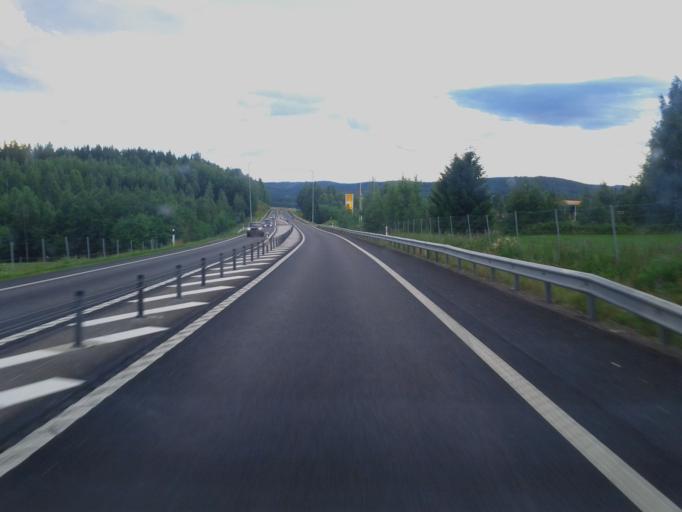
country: SE
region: Dalarna
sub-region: Borlange Kommun
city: Borlaenge
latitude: 60.4334
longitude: 15.3424
